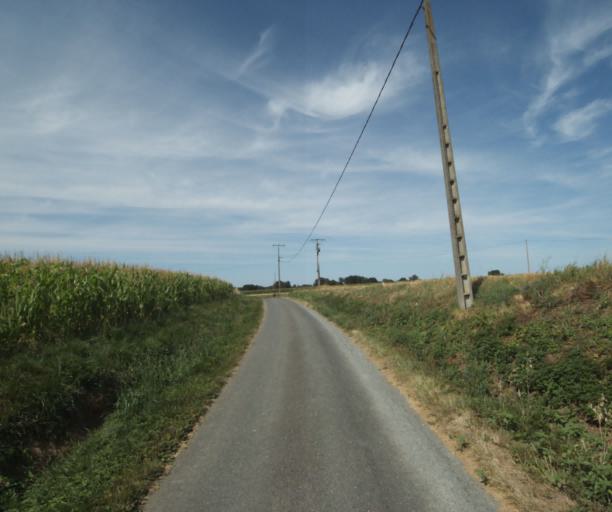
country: FR
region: Midi-Pyrenees
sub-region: Departement du Tarn
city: Soreze
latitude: 43.5102
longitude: 2.0738
